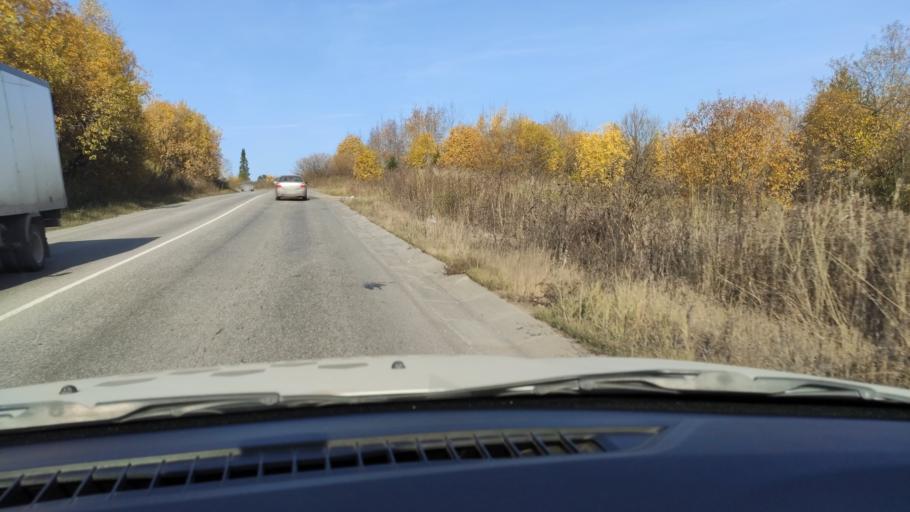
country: RU
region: Perm
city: Novyye Lyady
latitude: 58.0426
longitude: 56.5963
